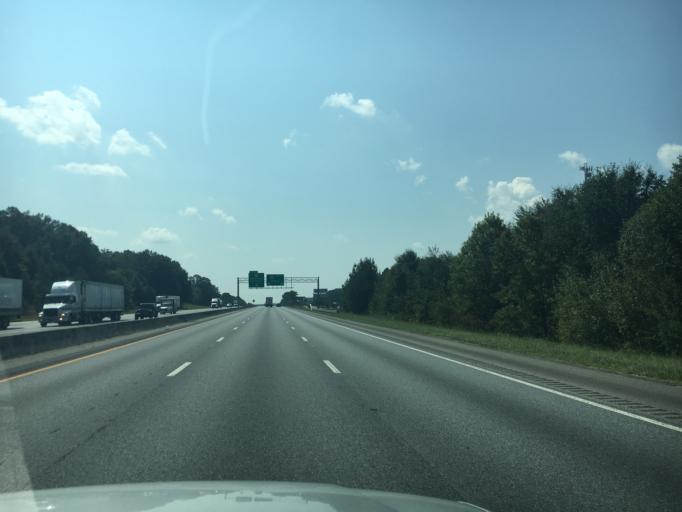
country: US
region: South Carolina
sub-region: Anderson County
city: Piedmont
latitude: 34.7076
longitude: -82.5003
